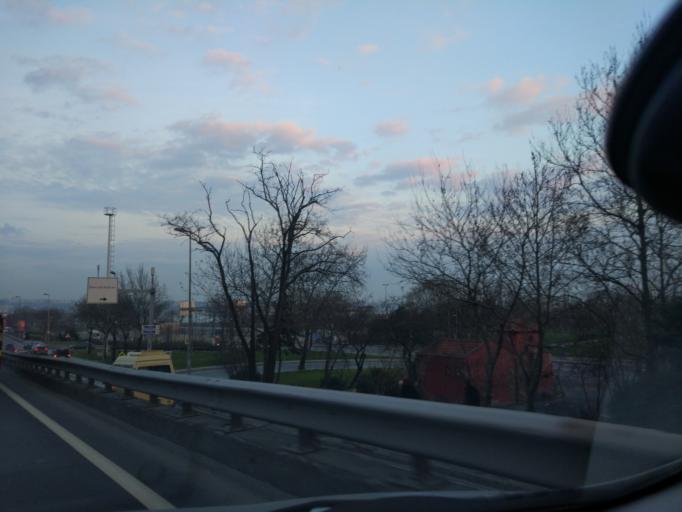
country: TR
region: Istanbul
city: Yakuplu
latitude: 40.9786
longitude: 28.7471
